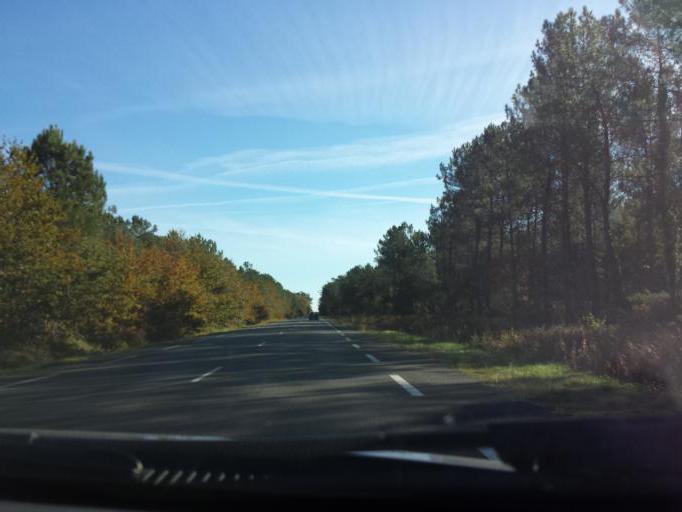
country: FR
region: Aquitaine
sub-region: Departement de la Gironde
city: Sainte-Helene
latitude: 44.9722
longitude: -0.9639
